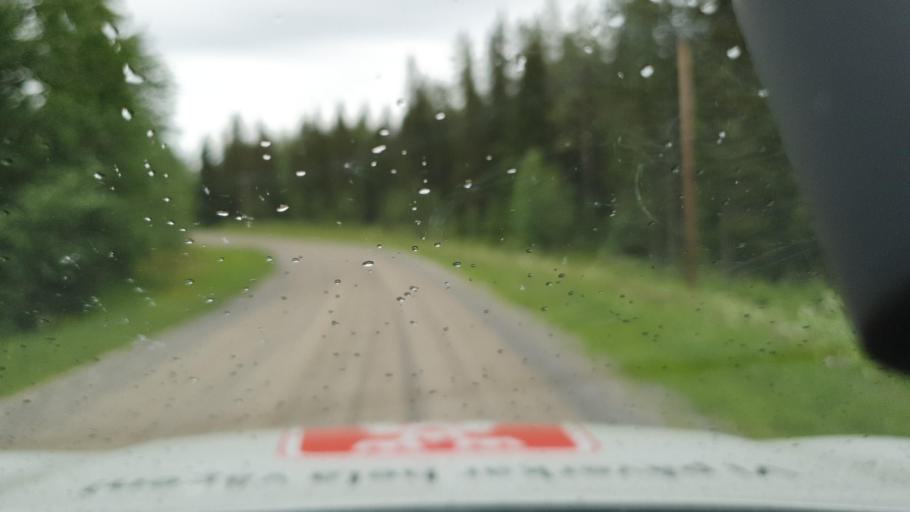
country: SE
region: Vaesterbotten
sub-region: Nordmalings Kommun
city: Nordmaling
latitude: 63.7531
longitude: 19.4977
